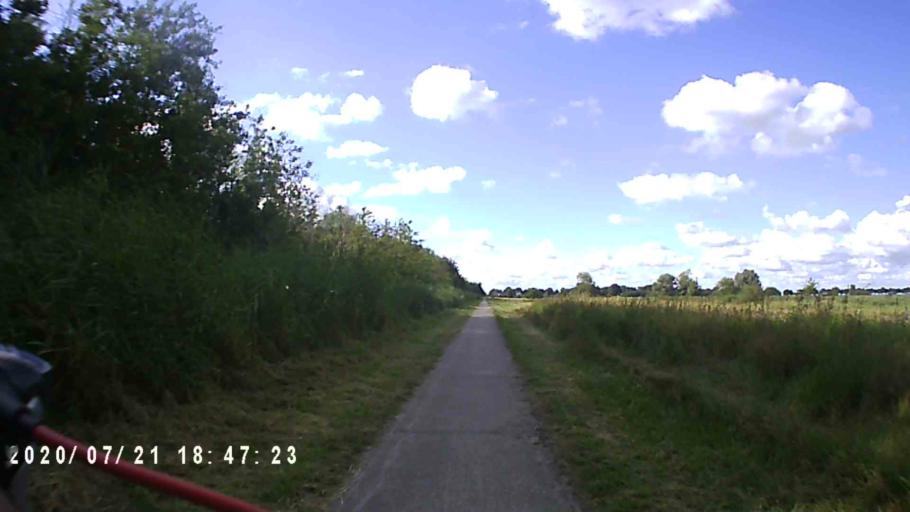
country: NL
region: Groningen
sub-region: Gemeente Hoogezand-Sappemeer
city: Hoogezand
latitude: 53.2127
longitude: 6.7482
